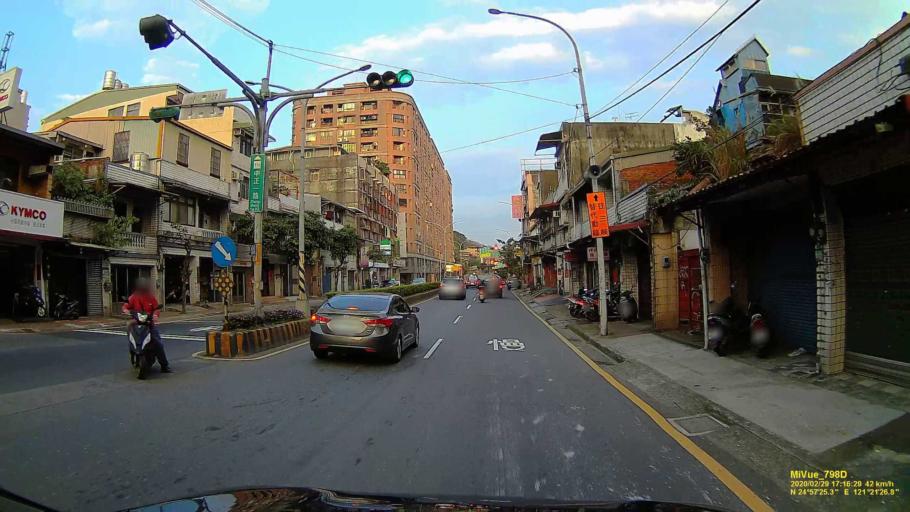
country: TW
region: Taiwan
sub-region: Taoyuan
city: Taoyuan
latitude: 24.9570
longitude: 121.3575
